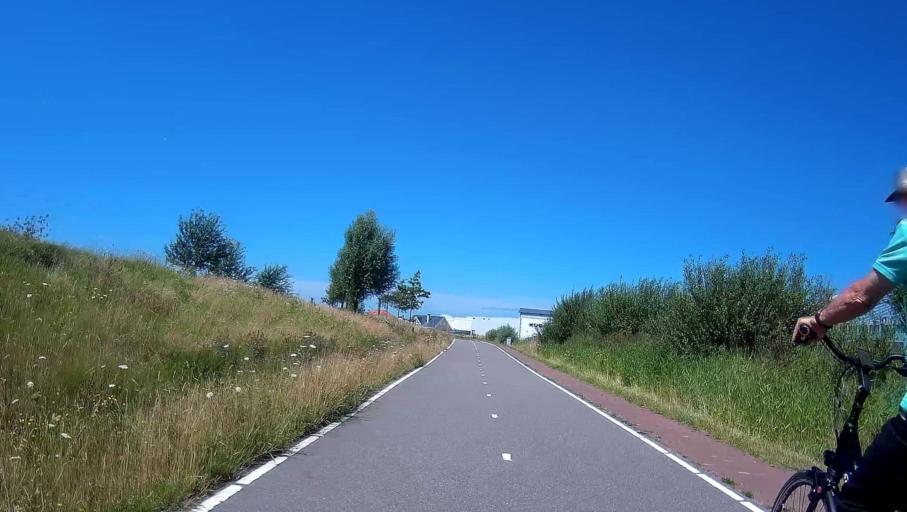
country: NL
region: South Holland
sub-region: Gemeente Westland
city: Monster
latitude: 52.0154
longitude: 4.1745
